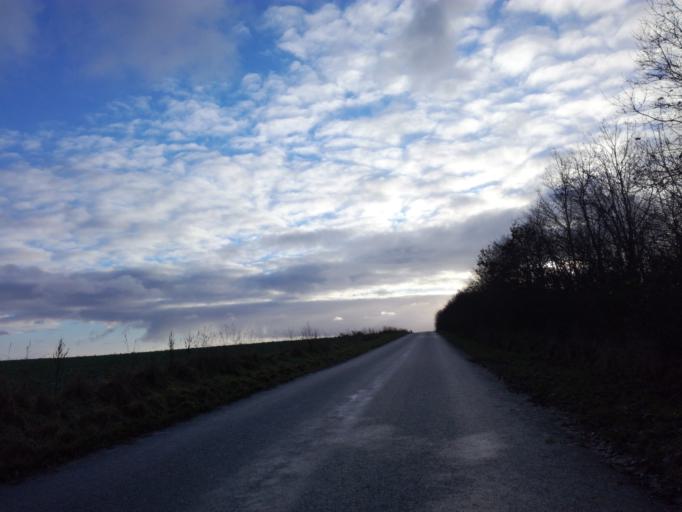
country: DK
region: South Denmark
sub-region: Fredericia Kommune
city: Taulov
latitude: 55.5677
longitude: 9.6050
